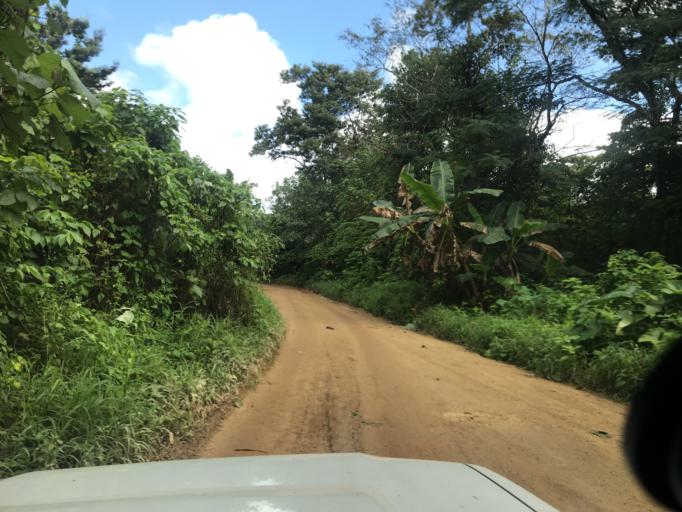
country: VU
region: Sanma
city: Luganville
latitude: -15.4728
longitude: 167.0803
